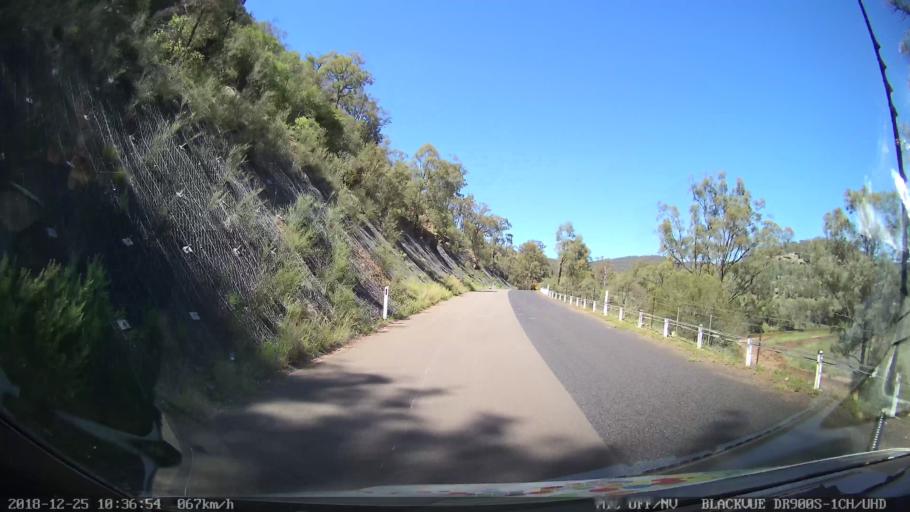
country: AU
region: New South Wales
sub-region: Upper Hunter Shire
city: Merriwa
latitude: -32.4086
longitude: 150.3828
